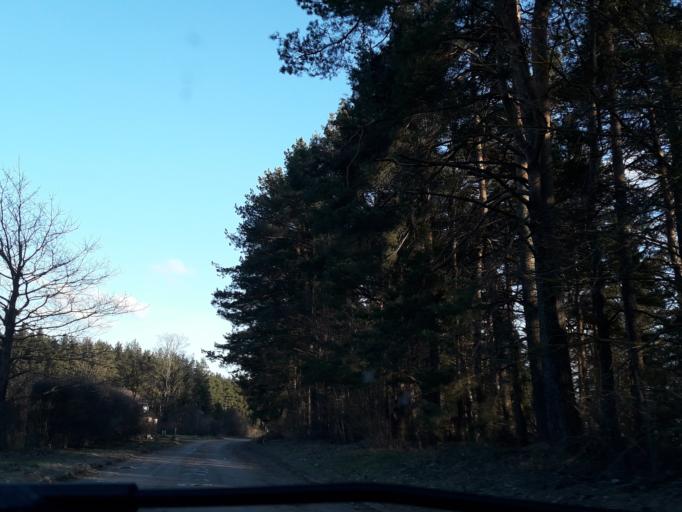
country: LV
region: Kekava
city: Kekava
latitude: 56.8607
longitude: 24.2182
